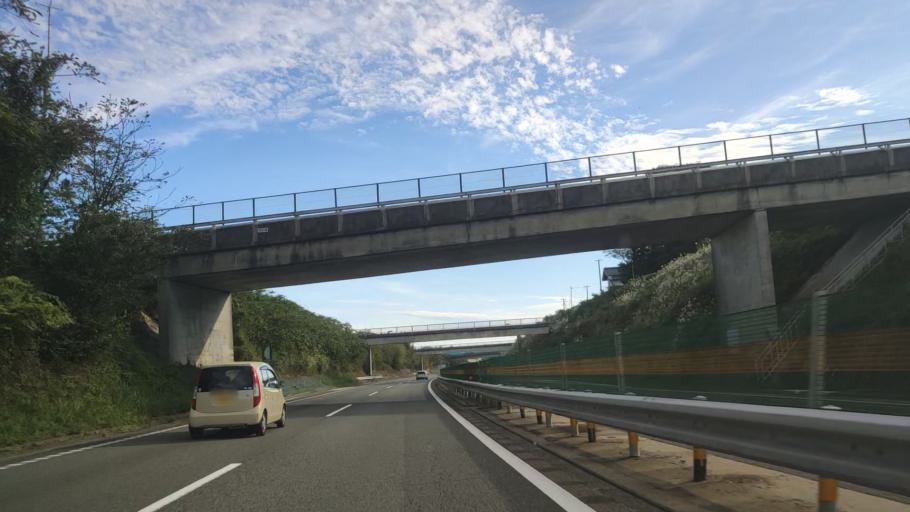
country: JP
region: Nagano
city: Ina
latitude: 35.6969
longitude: 137.9111
